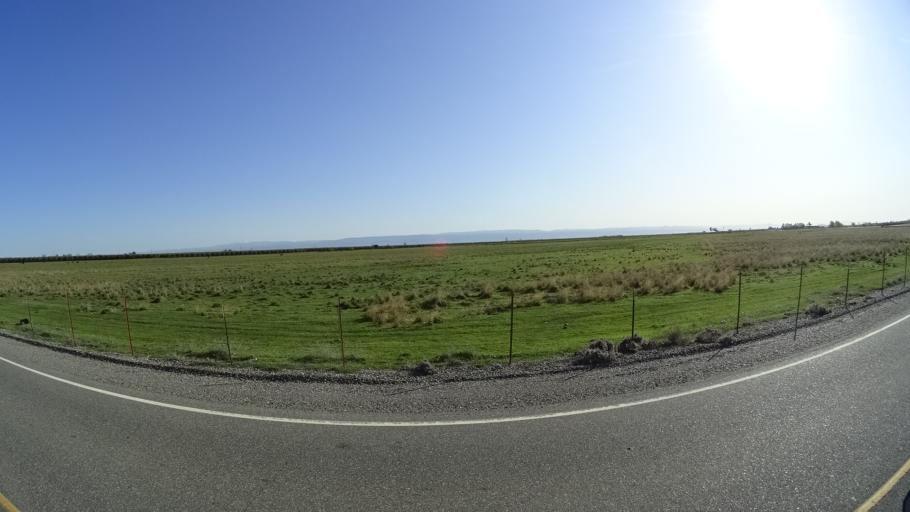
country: US
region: California
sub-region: Glenn County
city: Hamilton City
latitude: 39.7478
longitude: -122.0984
